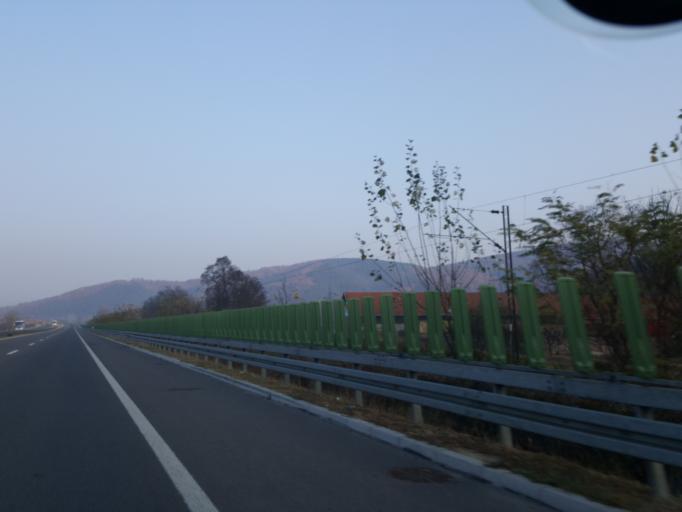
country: RS
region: Central Serbia
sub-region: Jablanicki Okrug
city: Vlasotince
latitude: 42.9021
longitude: 22.0508
